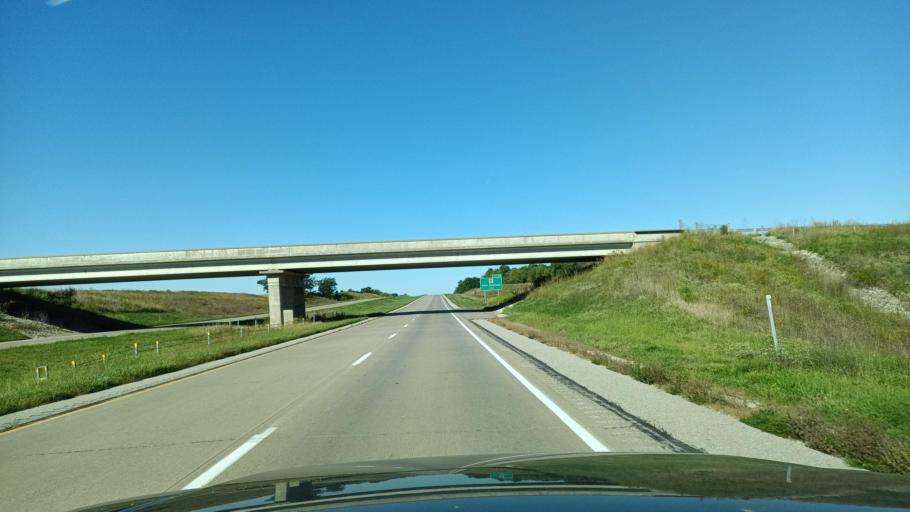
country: US
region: Iowa
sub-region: Lee County
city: Fort Madison
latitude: 40.6708
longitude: -91.3004
